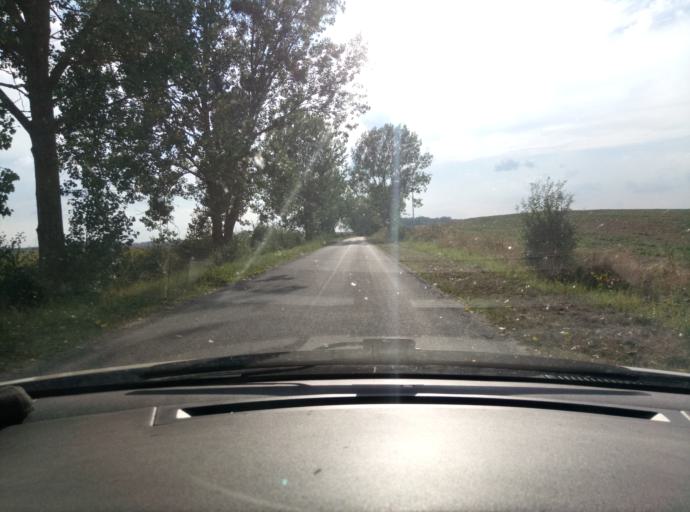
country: PL
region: Kujawsko-Pomorskie
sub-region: Powiat brodnicki
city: Jablonowo Pomorskie
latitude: 53.3883
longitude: 19.2074
